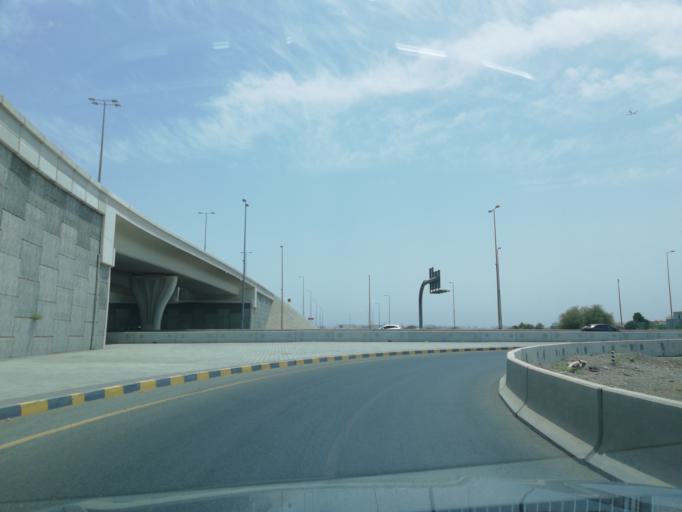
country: OM
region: Muhafazat Masqat
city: As Sib al Jadidah
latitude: 23.6662
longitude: 58.1606
